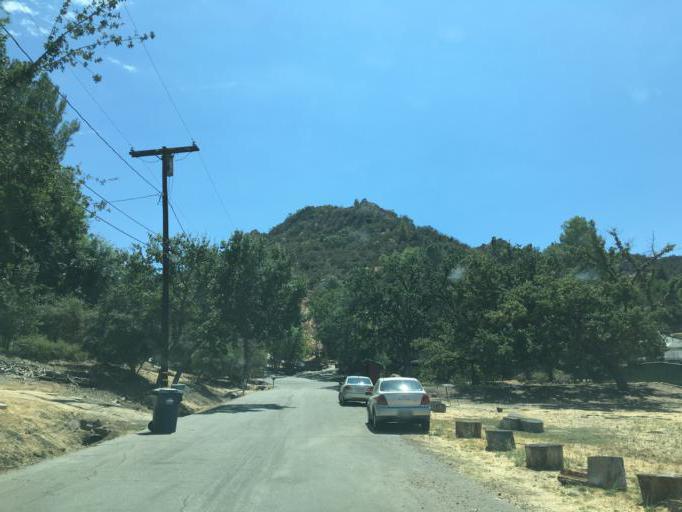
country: US
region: California
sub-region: Los Angeles County
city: Agoura Hills
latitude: 34.1051
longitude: -118.7589
